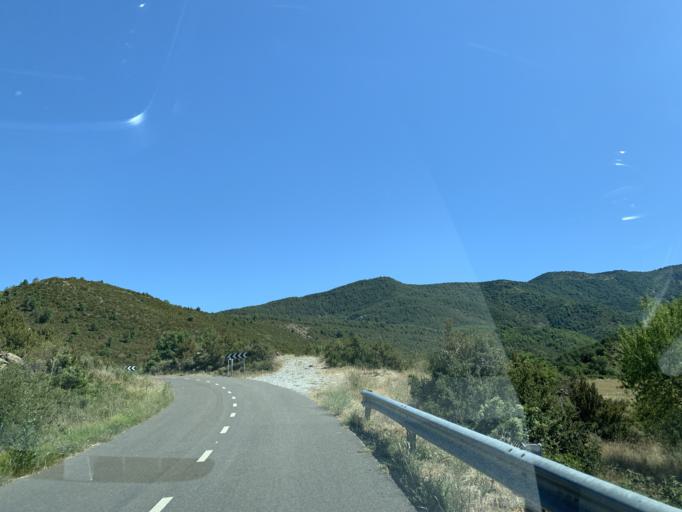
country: ES
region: Aragon
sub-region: Provincia de Huesca
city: Sabinanigo
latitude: 42.5442
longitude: -0.3162
